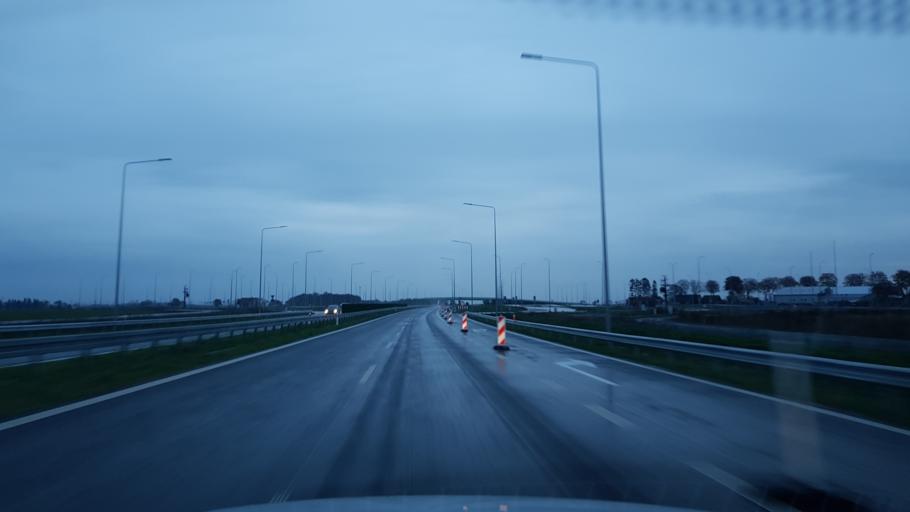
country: PL
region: West Pomeranian Voivodeship
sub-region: Powiat gryficki
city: Brojce
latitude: 53.9842
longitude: 15.4322
